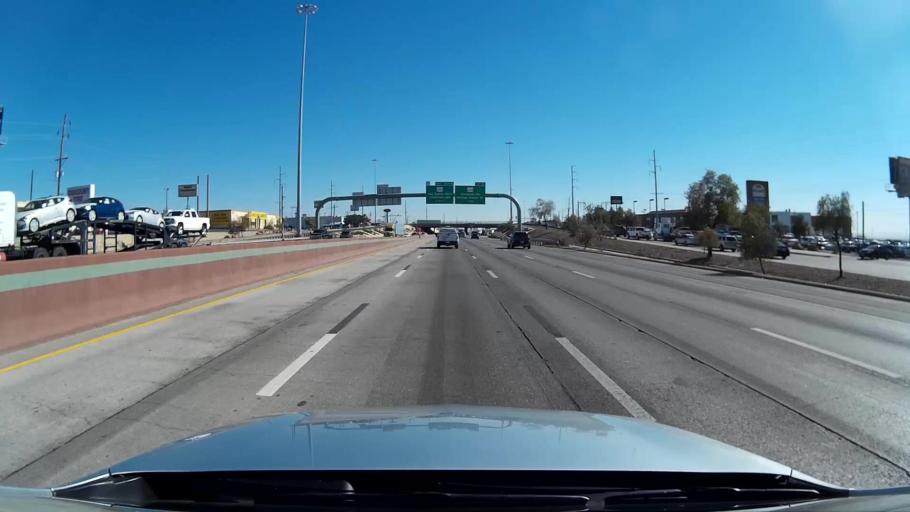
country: US
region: Texas
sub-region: El Paso County
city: Socorro
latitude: 31.7414
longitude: -106.3273
